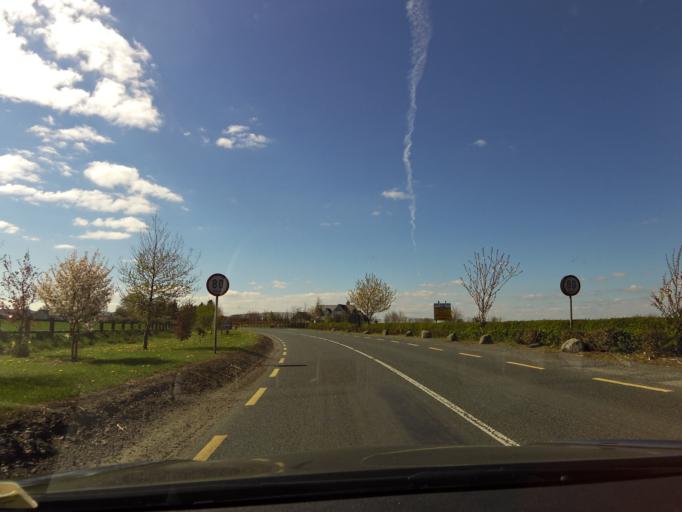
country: IE
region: Leinster
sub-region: Kildare
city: Athy
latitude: 52.9996
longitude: -7.0032
